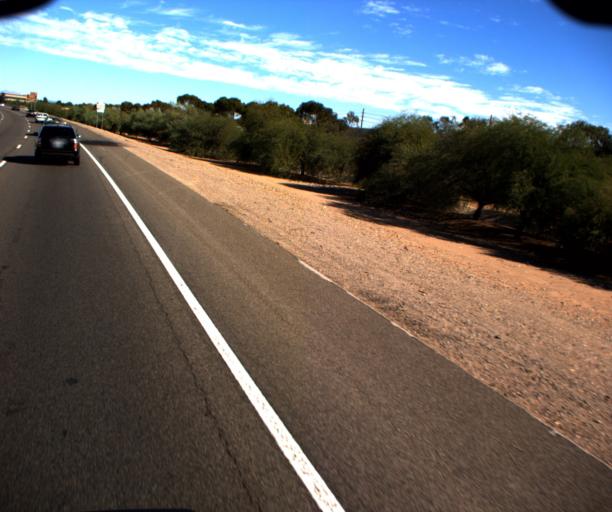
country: US
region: Arizona
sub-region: Maricopa County
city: Peoria
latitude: 33.6174
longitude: -112.2392
